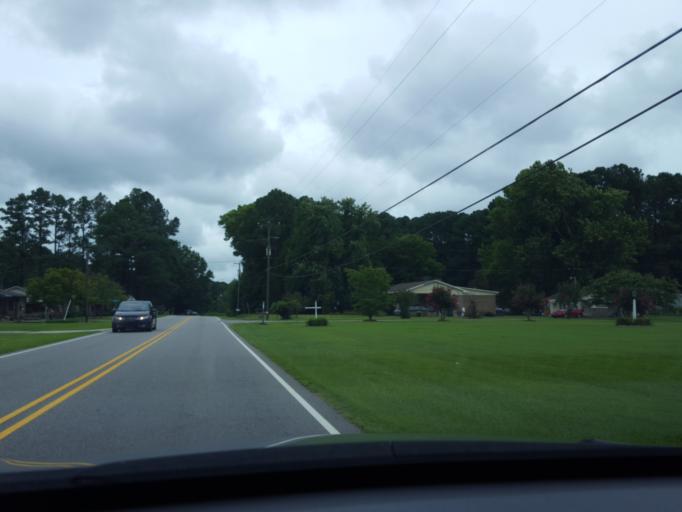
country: US
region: North Carolina
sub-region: Martin County
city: Williamston
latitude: 35.7970
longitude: -76.9022
